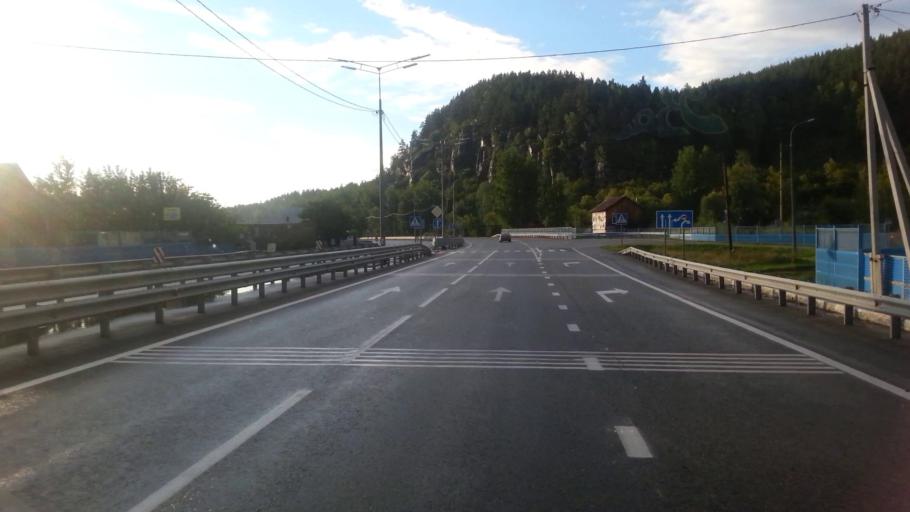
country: RU
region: Altay
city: Souzga
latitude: 51.9174
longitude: 85.8599
